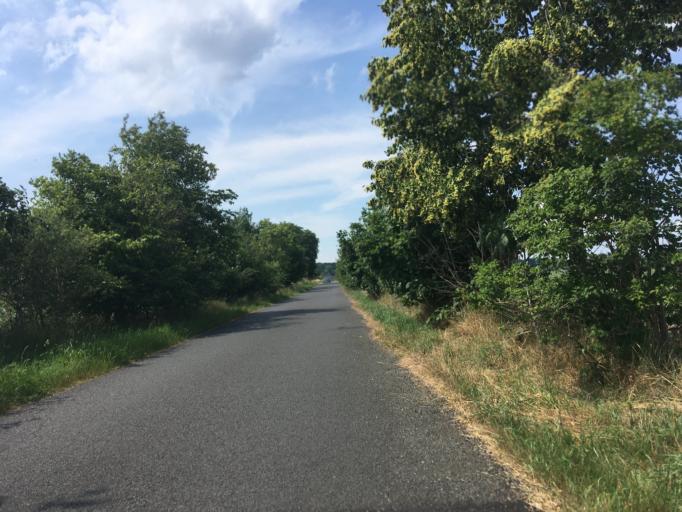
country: DE
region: Saxony-Anhalt
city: Quellendorf
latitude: 51.7786
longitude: 12.1172
